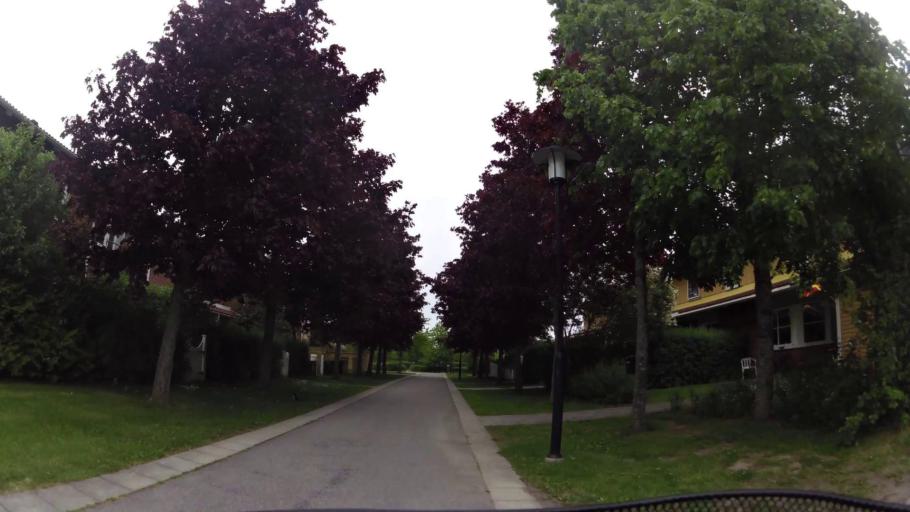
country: SE
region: OEstergoetland
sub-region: Linkopings Kommun
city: Malmslatt
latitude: 58.3841
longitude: 15.5570
